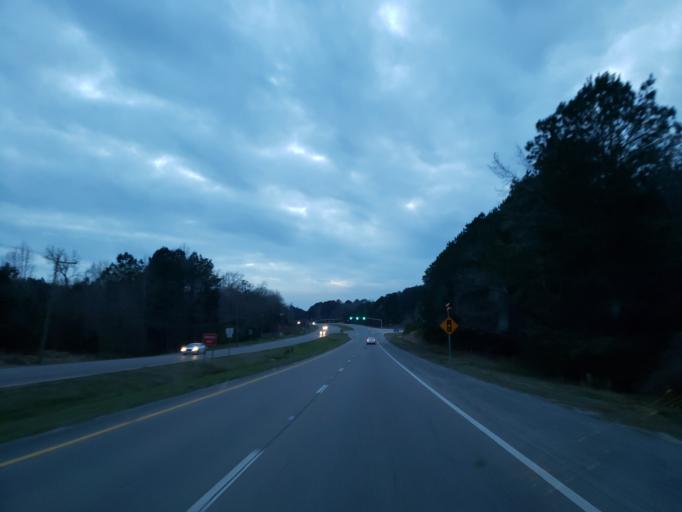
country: US
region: Mississippi
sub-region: Lauderdale County
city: Marion
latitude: 32.3669
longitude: -88.6504
